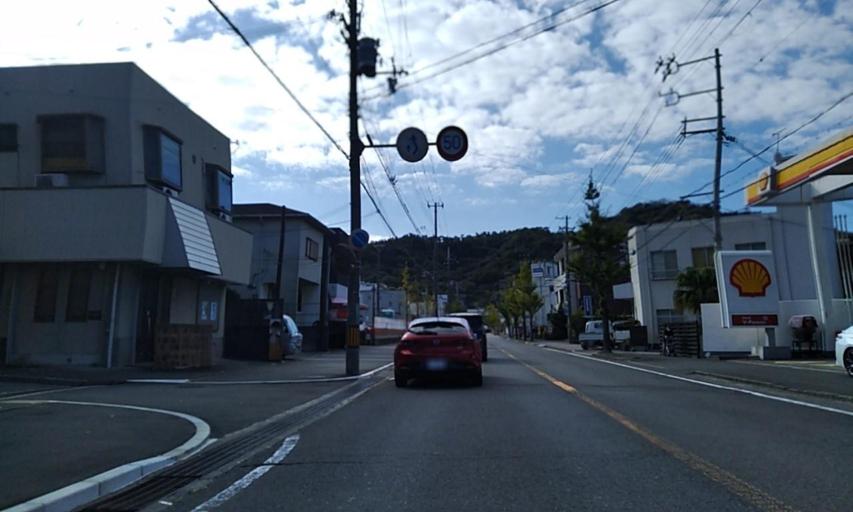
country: JP
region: Wakayama
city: Minato
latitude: 34.1949
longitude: 135.1589
